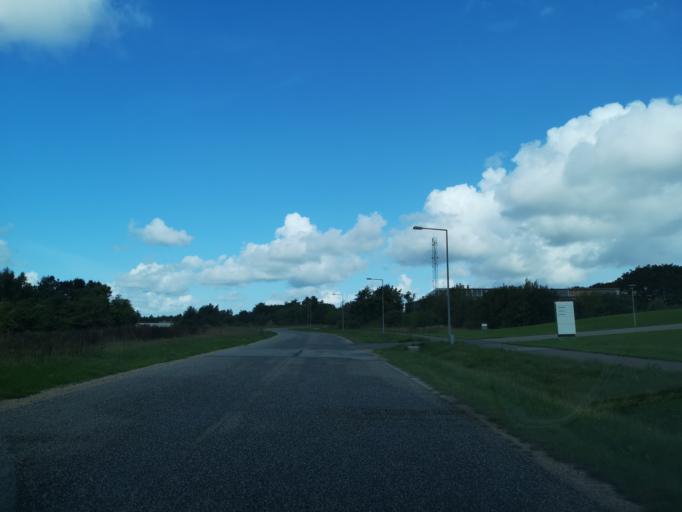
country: DK
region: Central Jutland
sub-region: Holstebro Kommune
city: Holstebro
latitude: 56.3382
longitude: 8.6398
